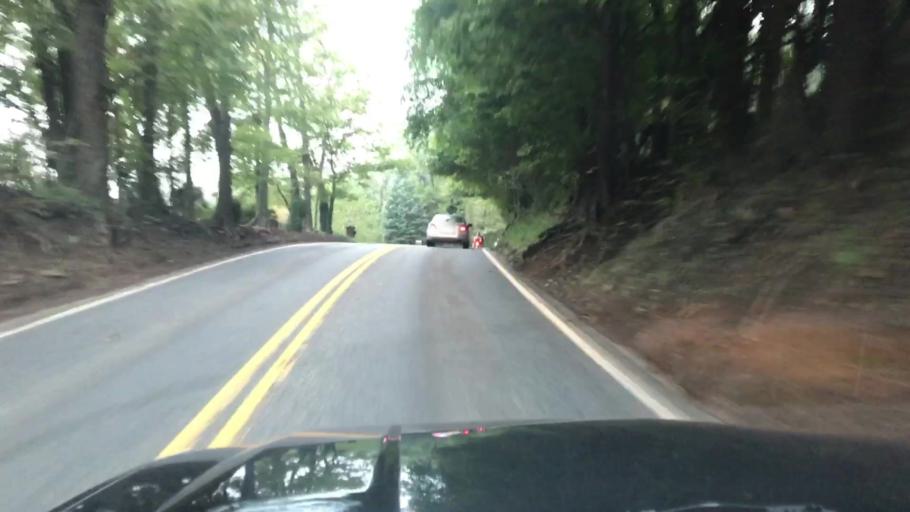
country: US
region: Pennsylvania
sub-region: Cumberland County
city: Shiremanstown
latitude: 40.1869
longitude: -76.9351
